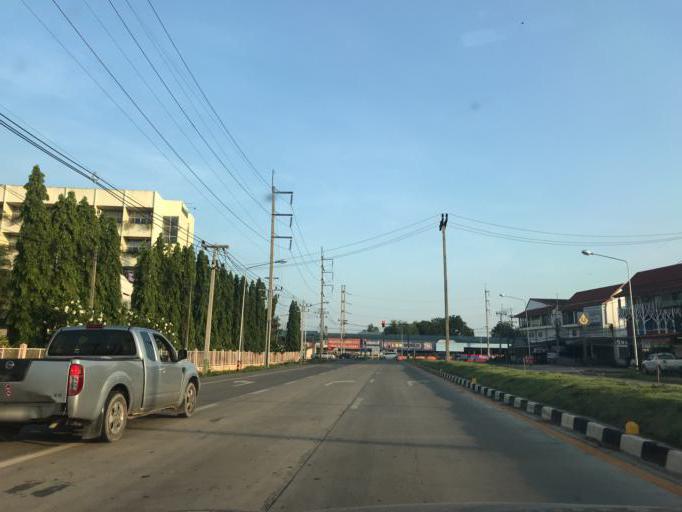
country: TH
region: Phayao
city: Chiang Kham
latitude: 19.5188
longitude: 100.2955
